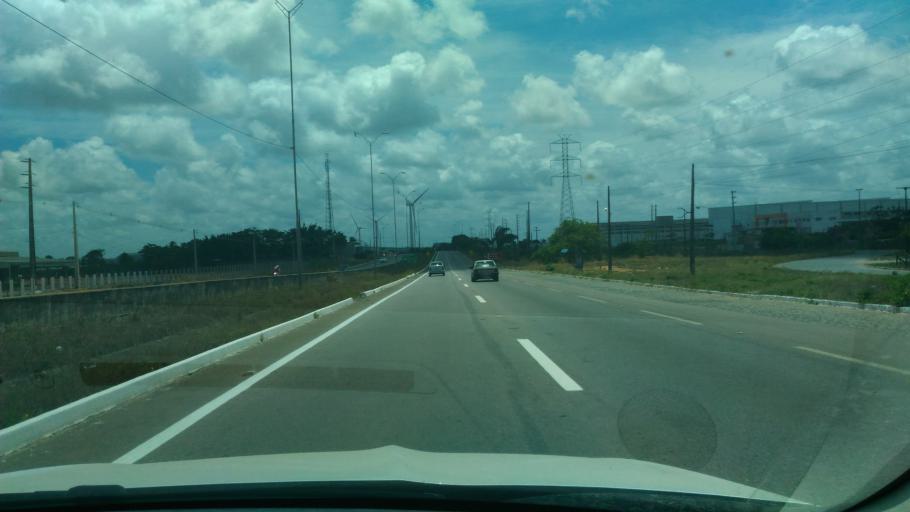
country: BR
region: Paraiba
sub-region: Conde
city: Conde
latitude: -7.2532
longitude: -34.9337
